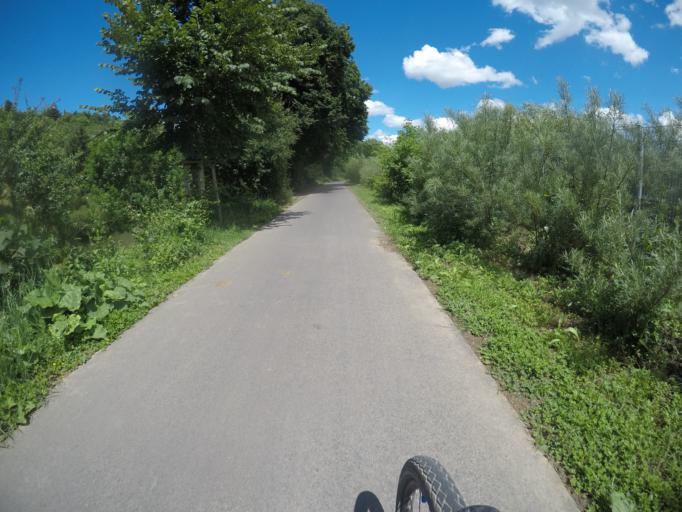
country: DE
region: Baden-Wuerttemberg
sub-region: Tuebingen Region
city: Tuebingen
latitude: 48.5090
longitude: 9.0355
